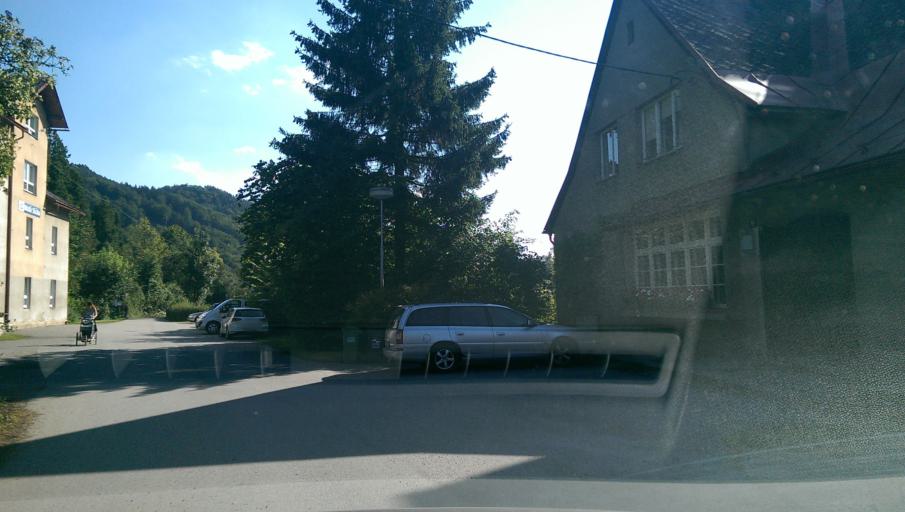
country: CZ
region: Liberecky
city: Mala Skala
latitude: 50.6345
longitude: 15.1916
